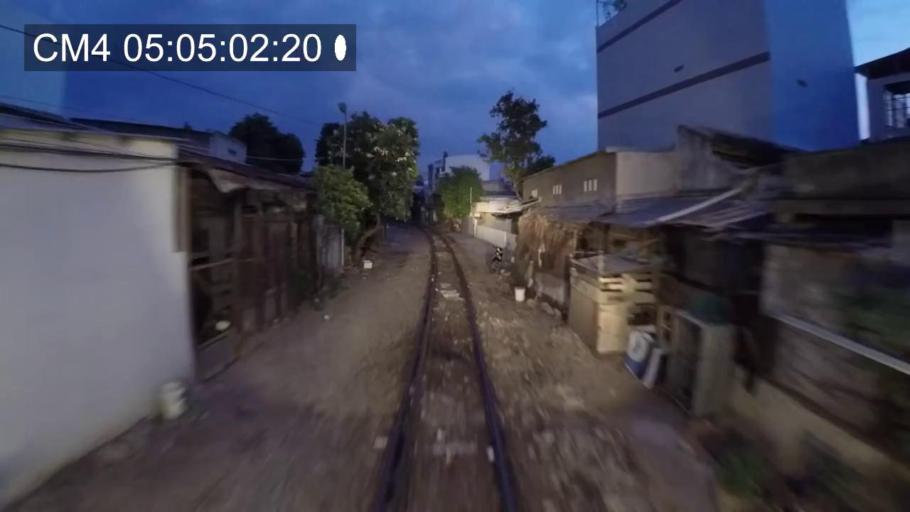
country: VN
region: Khanh Hoa
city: Nha Trang
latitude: 12.2683
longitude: 109.1740
